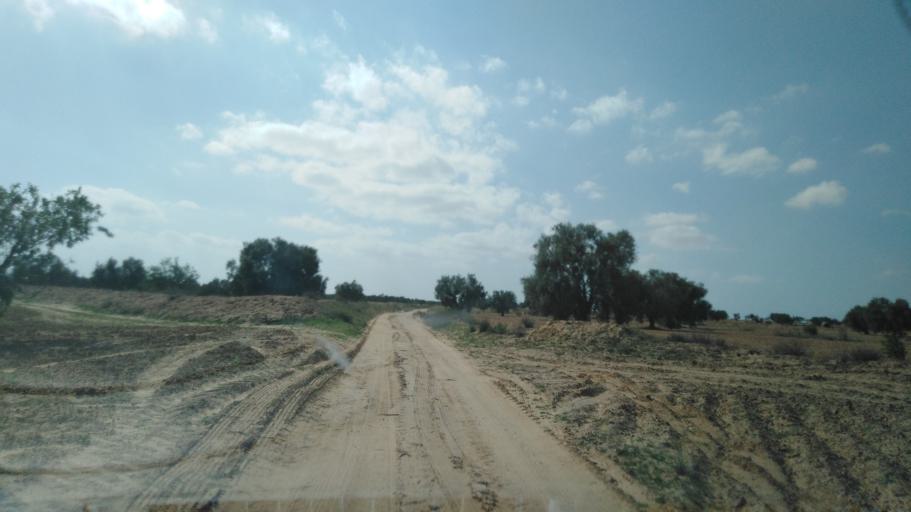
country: TN
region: Safaqis
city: Bi'r `Ali Bin Khalifah
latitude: 34.7990
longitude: 10.3853
